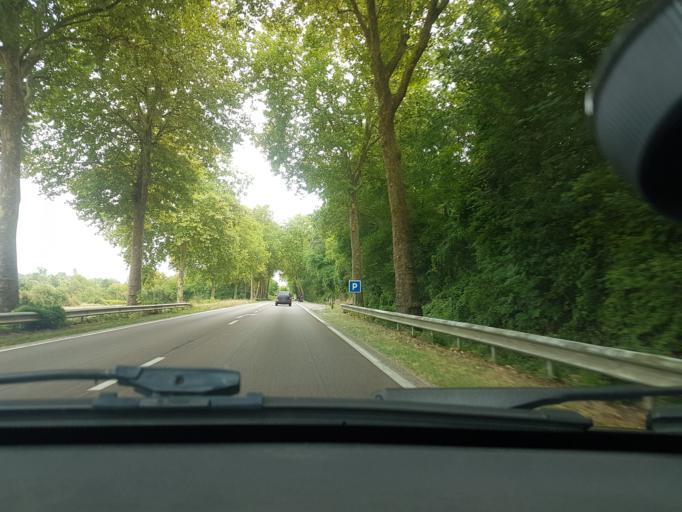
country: FR
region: Bourgogne
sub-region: Departement de l'Yonne
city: Champs-sur-Yonne
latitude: 47.7131
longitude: 3.6208
